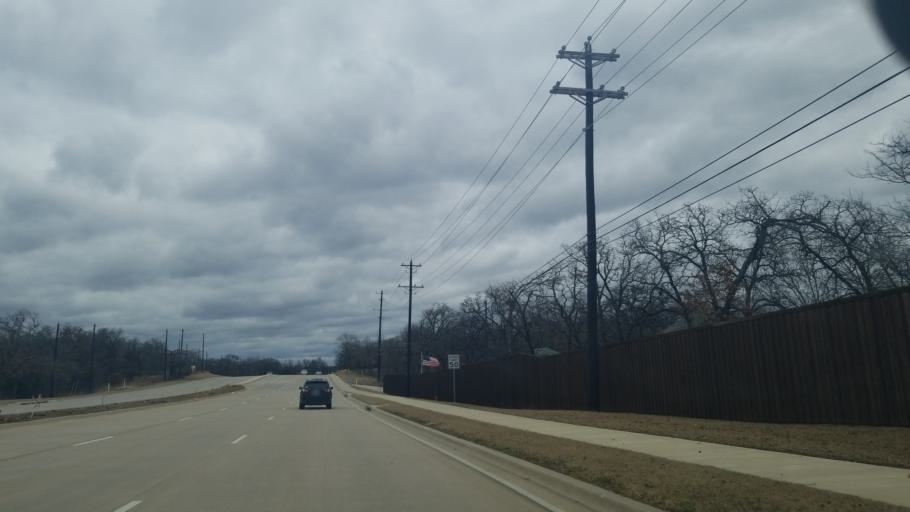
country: US
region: Texas
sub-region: Denton County
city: Bartonville
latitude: 33.0447
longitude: -97.1508
